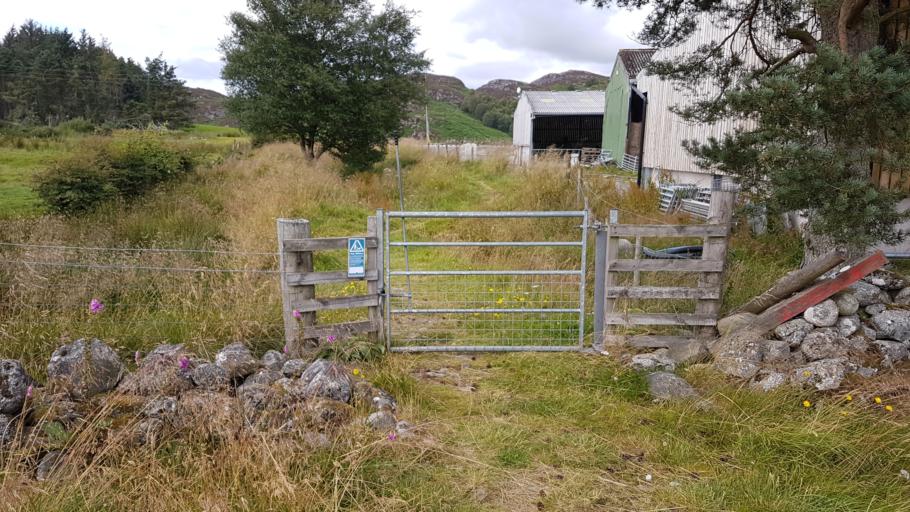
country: GB
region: Scotland
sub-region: Highland
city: Beauly
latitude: 57.2181
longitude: -4.5025
